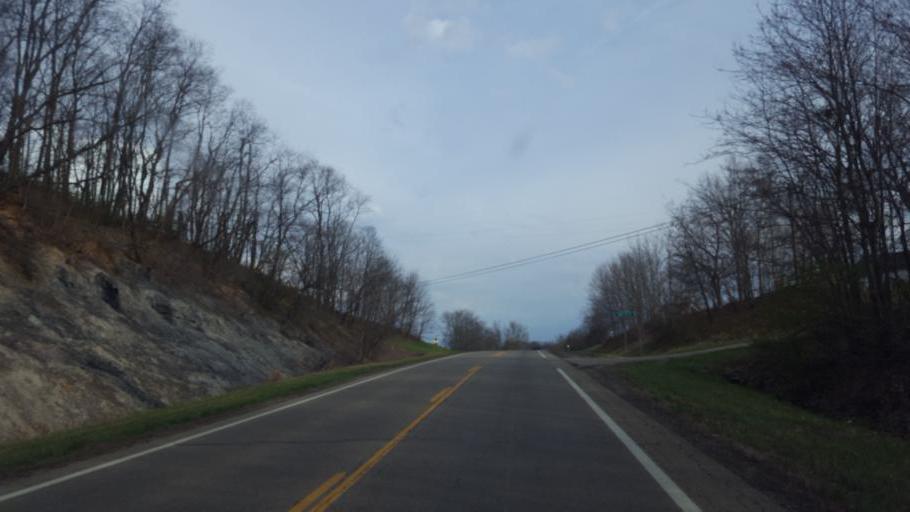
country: US
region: Ohio
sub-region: Coshocton County
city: Coshocton
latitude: 40.2346
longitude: -81.8534
